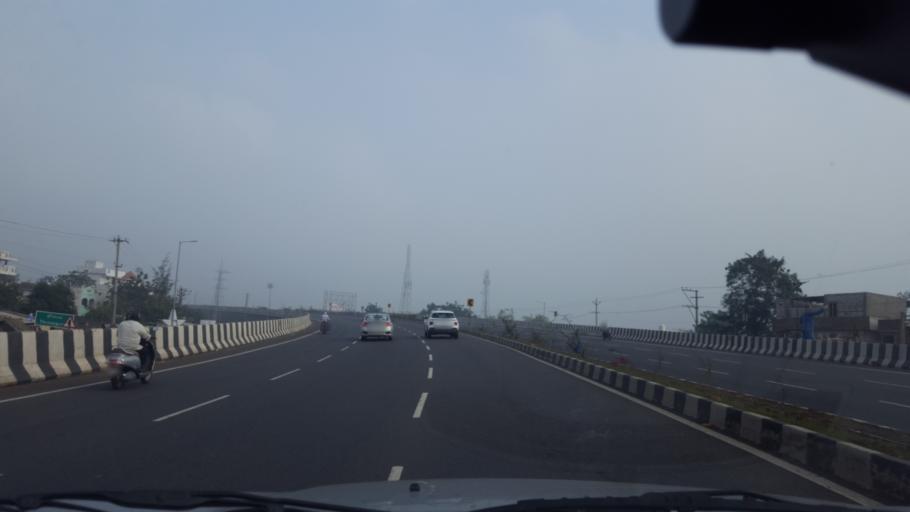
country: IN
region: Andhra Pradesh
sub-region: Prakasam
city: Ongole
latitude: 15.5500
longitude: 80.0563
